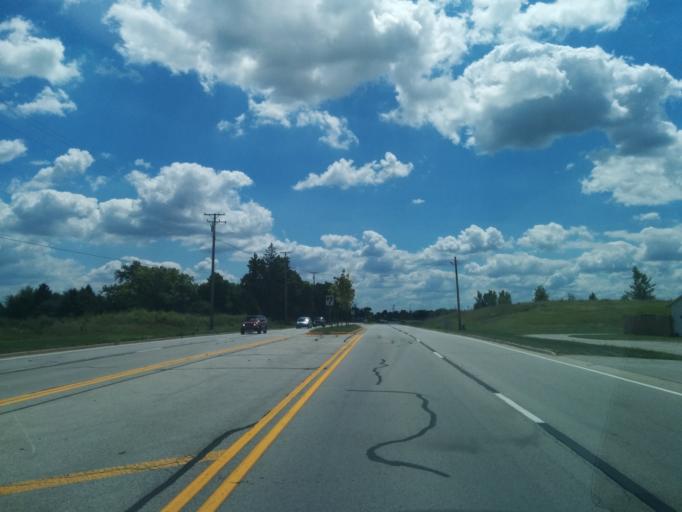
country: US
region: Illinois
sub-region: Will County
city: Plainfield
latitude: 41.6855
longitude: -88.1662
